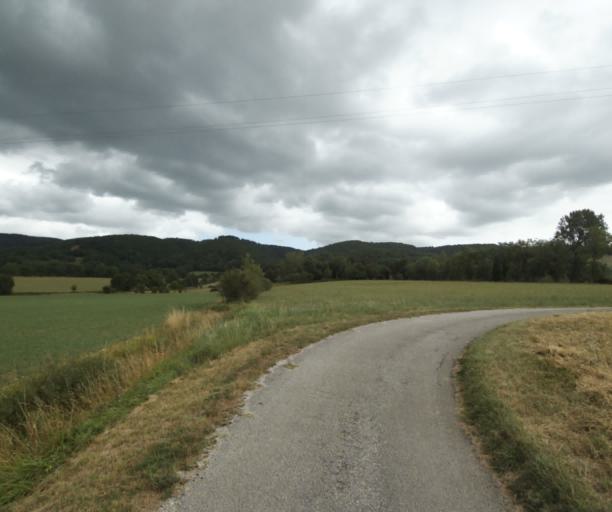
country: FR
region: Midi-Pyrenees
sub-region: Departement du Tarn
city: Soreze
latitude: 43.4618
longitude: 2.0833
